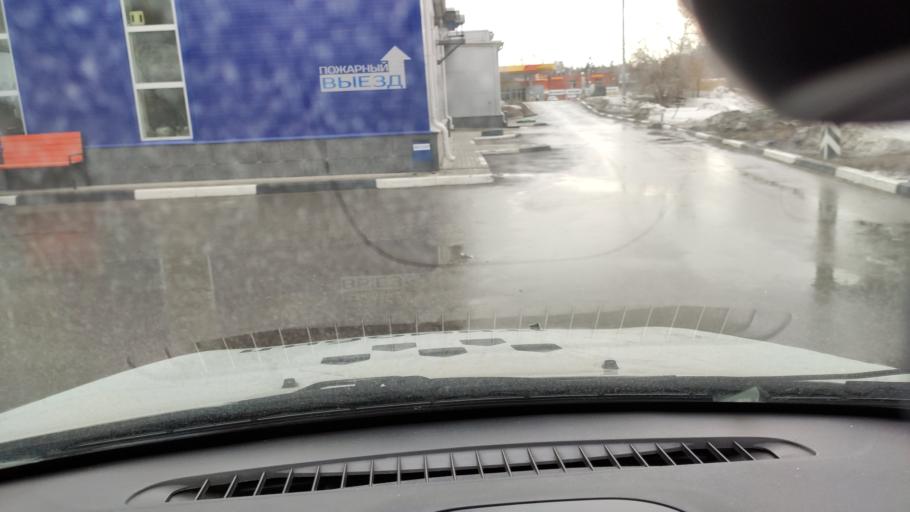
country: RU
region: Samara
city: Zhigulevsk
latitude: 53.4987
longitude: 49.4718
